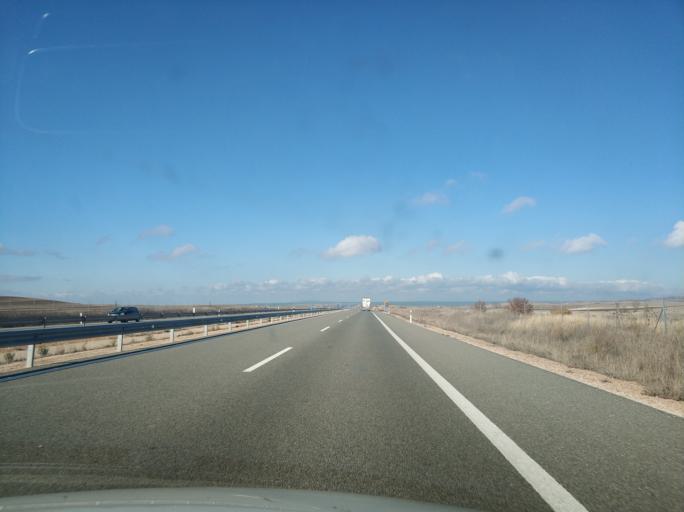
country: ES
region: Castille and Leon
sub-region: Provincia de Soria
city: Coscurita
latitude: 41.4007
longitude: -2.4774
